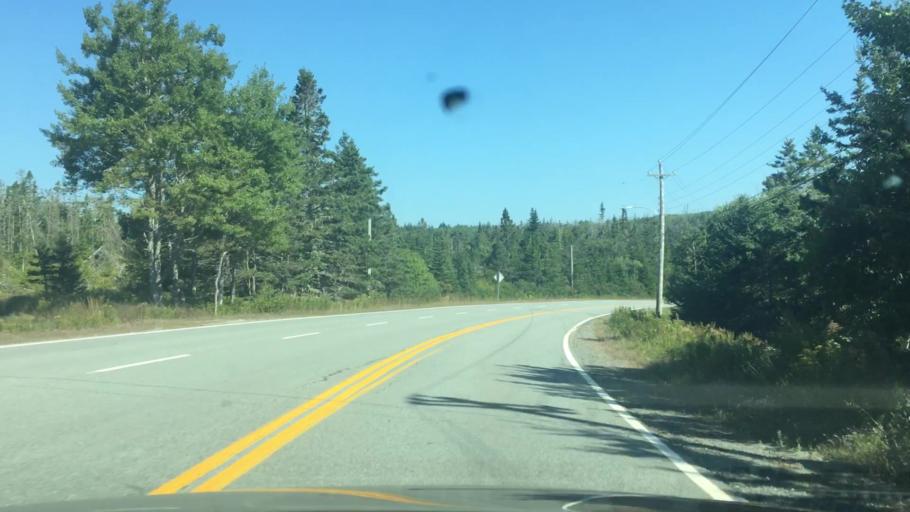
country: CA
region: Nova Scotia
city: New Glasgow
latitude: 44.8127
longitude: -62.6410
